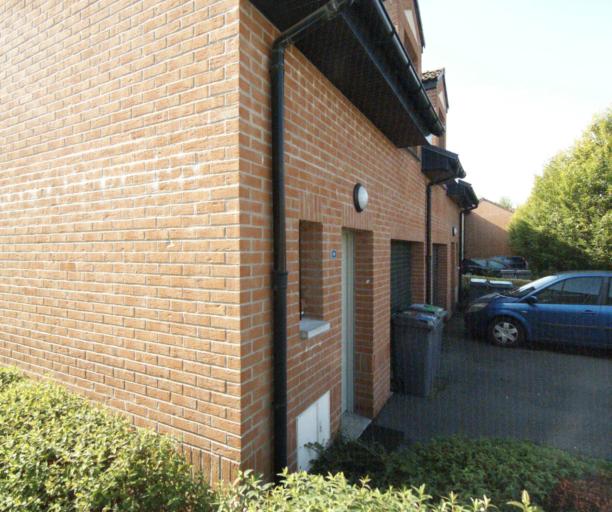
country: FR
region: Nord-Pas-de-Calais
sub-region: Departement du Nord
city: Perenchies
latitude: 50.6677
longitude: 2.9773
